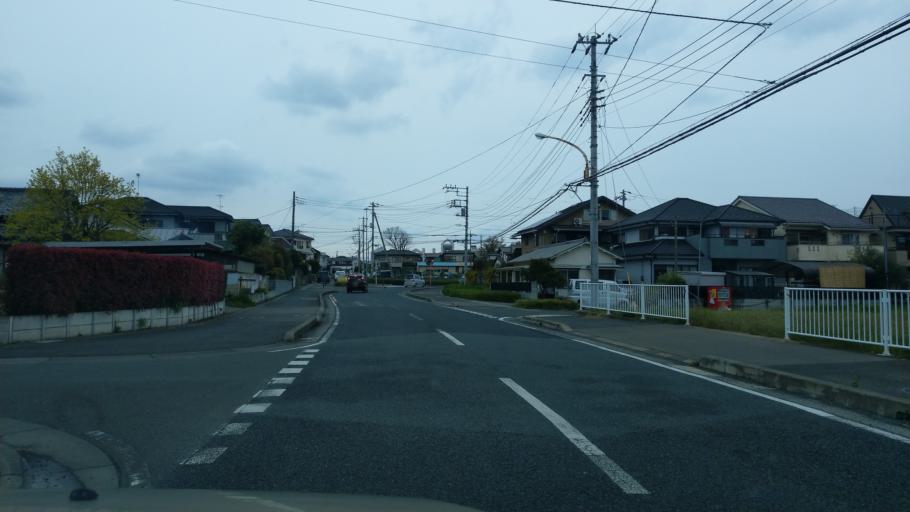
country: JP
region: Saitama
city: Ageoshimo
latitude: 35.9289
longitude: 139.5837
